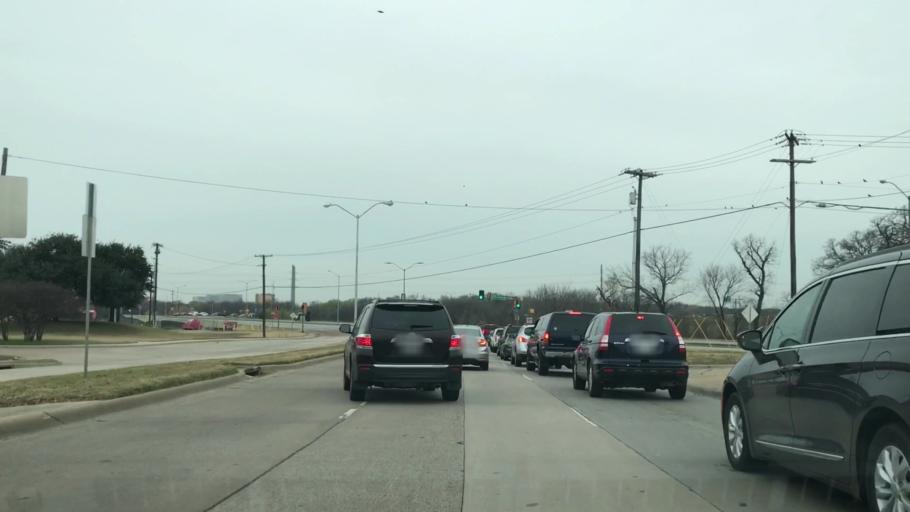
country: US
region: Texas
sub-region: Dallas County
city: University Park
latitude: 32.8507
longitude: -96.8773
